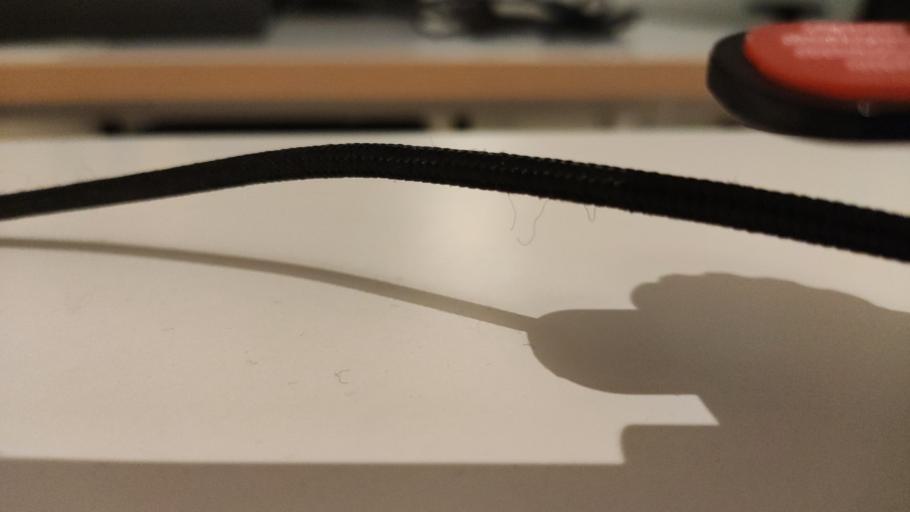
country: RU
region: Moskovskaya
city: Orekhovo-Zuyevo
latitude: 55.8342
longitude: 38.9688
